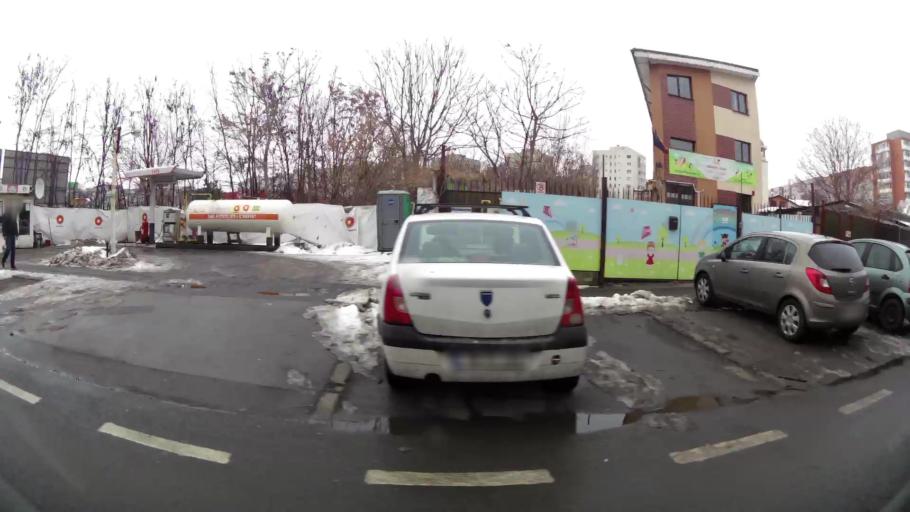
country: RO
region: Ilfov
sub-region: Comuna Popesti-Leordeni
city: Popesti-Leordeni
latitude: 44.4165
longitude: 26.1686
